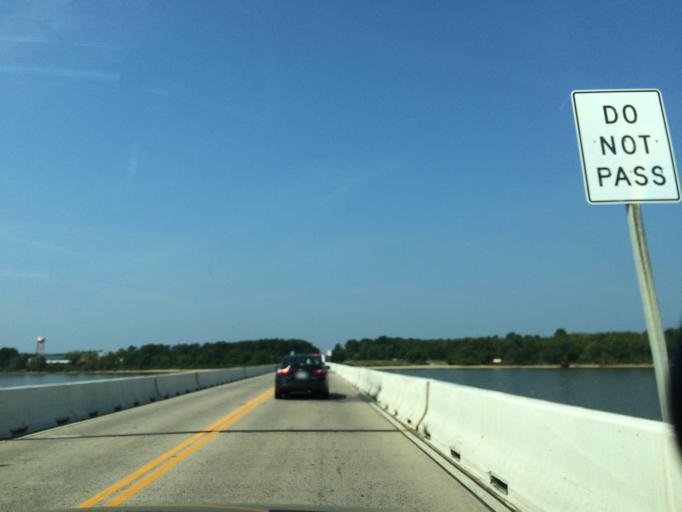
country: US
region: Virginia
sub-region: King George County
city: Dahlgren
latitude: 38.3600
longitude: -77.0093
